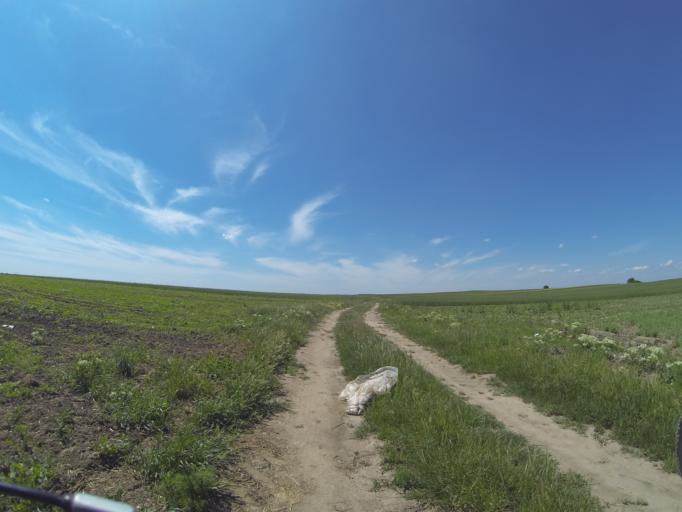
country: RO
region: Dolj
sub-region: Comuna Leu
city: Leu
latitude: 44.2153
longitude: 24.0222
